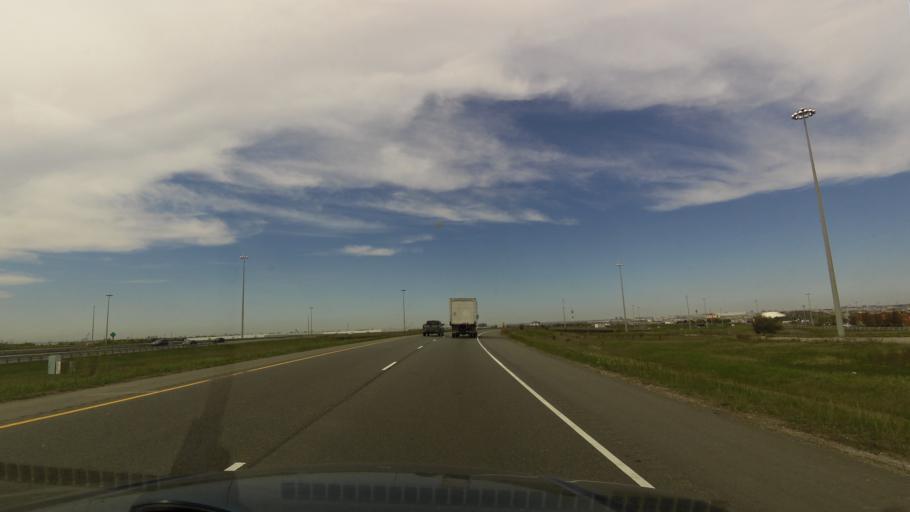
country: CA
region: Ontario
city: Mississauga
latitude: 43.6376
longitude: -79.6547
